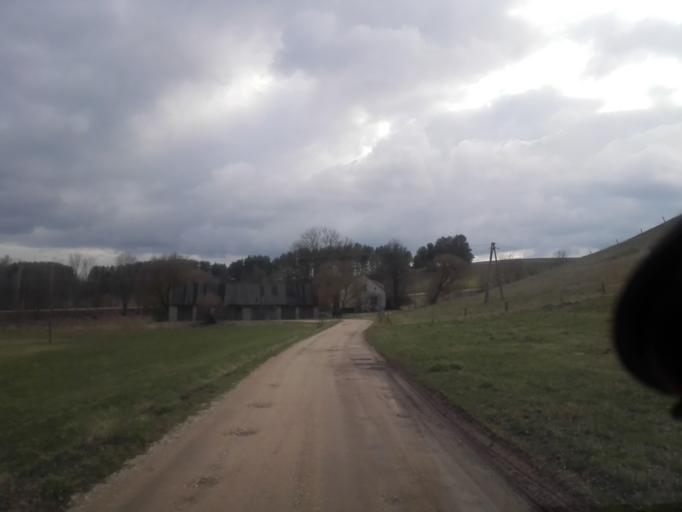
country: PL
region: Podlasie
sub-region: Suwalki
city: Suwalki
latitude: 54.2195
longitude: 22.8096
